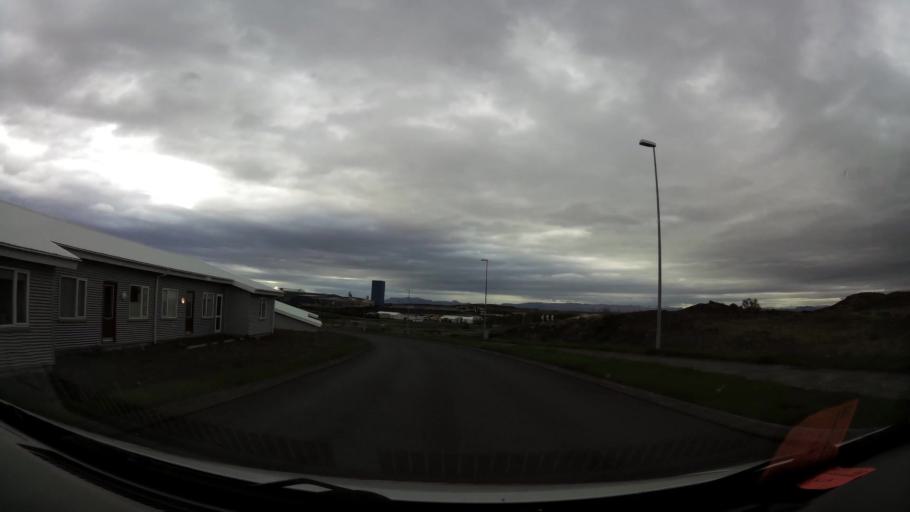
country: IS
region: West
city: Borgarnes
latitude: 64.5573
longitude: -21.8958
